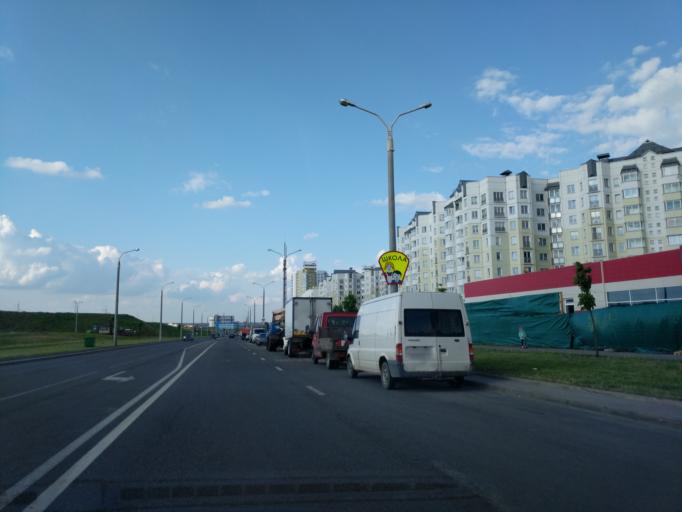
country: BY
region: Minsk
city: Zhdanovichy
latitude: 53.9249
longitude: 27.4210
